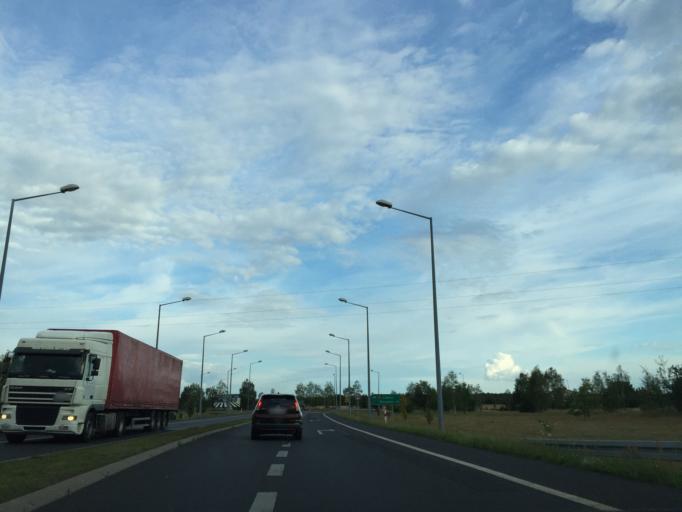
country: PL
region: Lublin Voivodeship
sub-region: Powiat lubartowski
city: Lubartow
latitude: 51.4347
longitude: 22.5948
